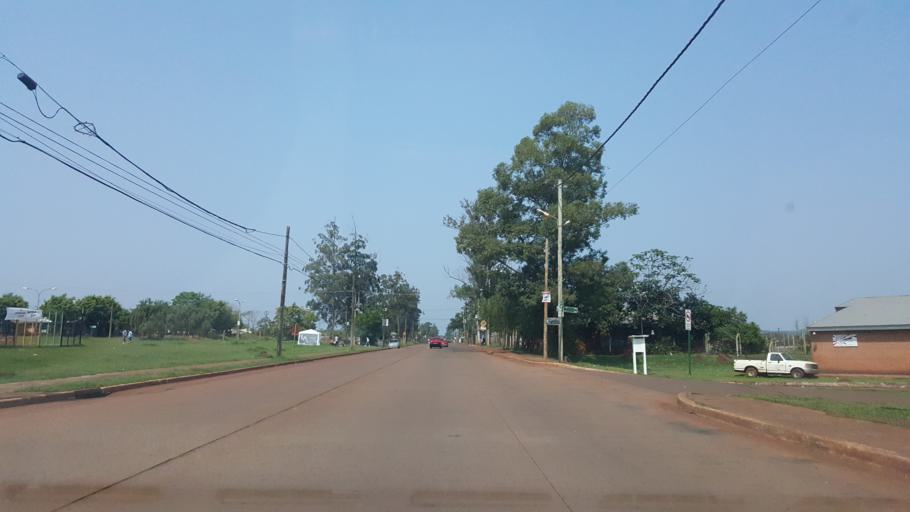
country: AR
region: Misiones
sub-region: Departamento de Capital
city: Posadas
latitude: -27.4068
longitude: -55.9538
